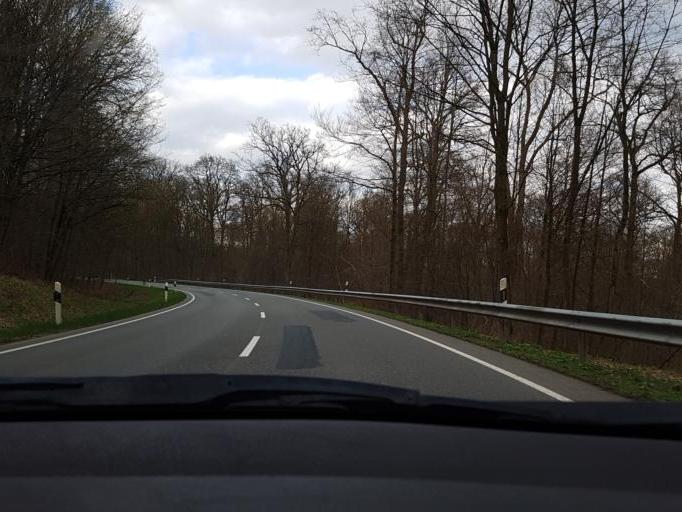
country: DE
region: Lower Saxony
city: Bodenfelde
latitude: 51.6898
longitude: 9.5309
